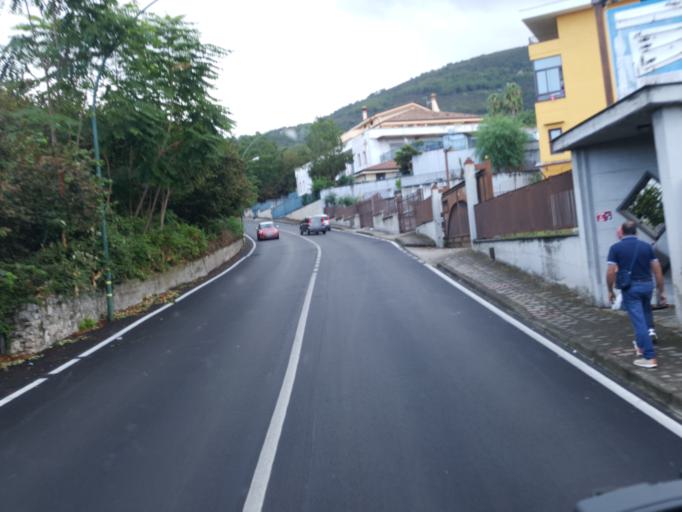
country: IT
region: Campania
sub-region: Provincia di Napoli
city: Carbonara di Nola
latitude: 40.8790
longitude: 14.5805
